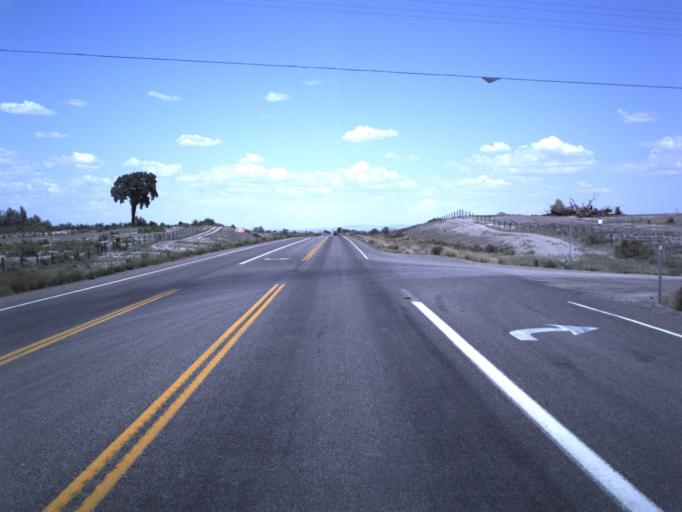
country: US
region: Utah
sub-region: Emery County
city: Castle Dale
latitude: 39.2205
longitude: -110.9977
